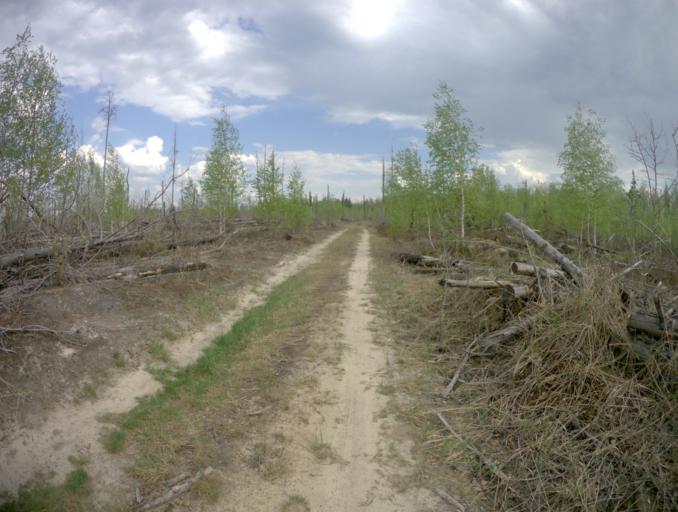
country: RU
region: Ivanovo
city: Talitsy
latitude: 56.4468
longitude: 42.2390
